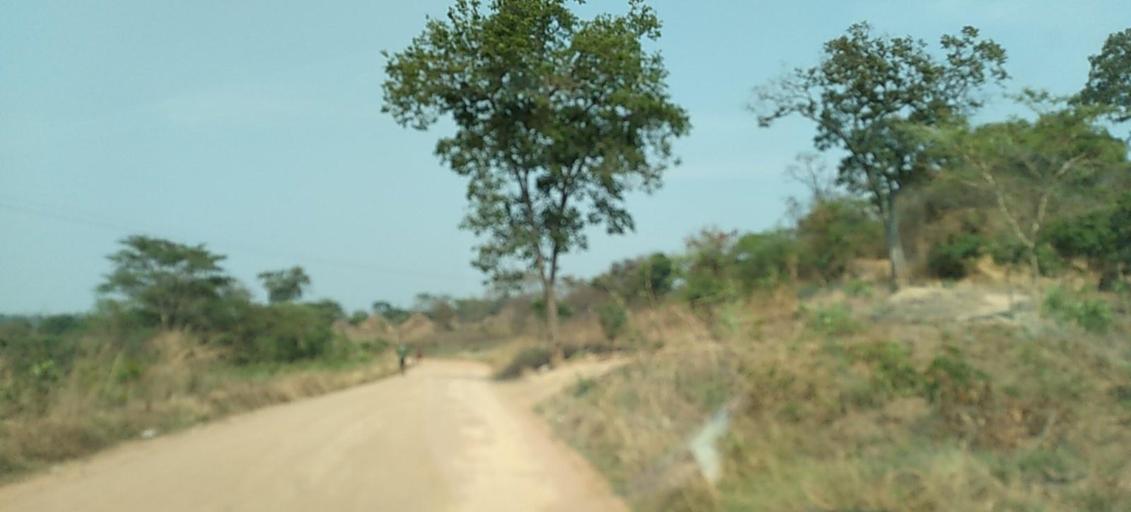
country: ZM
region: Copperbelt
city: Chililabombwe
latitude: -12.3371
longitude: 27.7234
